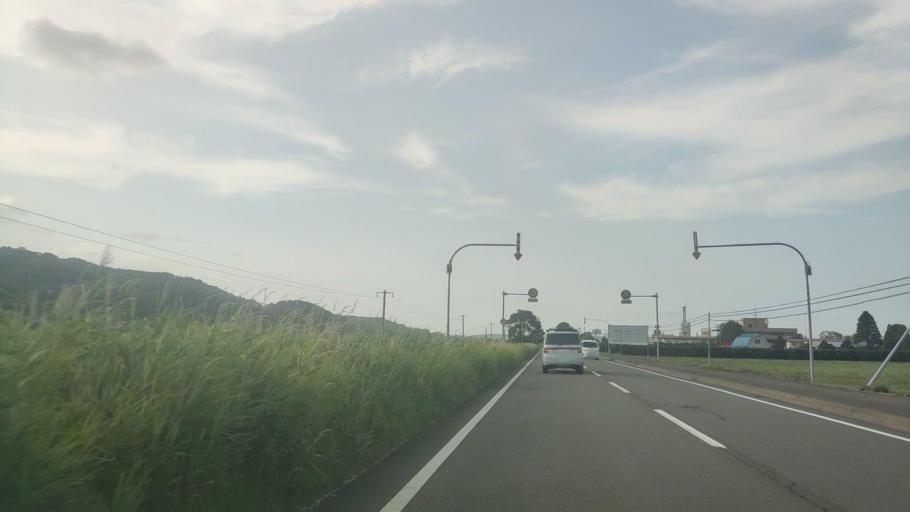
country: JP
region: Hokkaido
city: Iwamizawa
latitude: 42.9958
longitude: 141.7899
